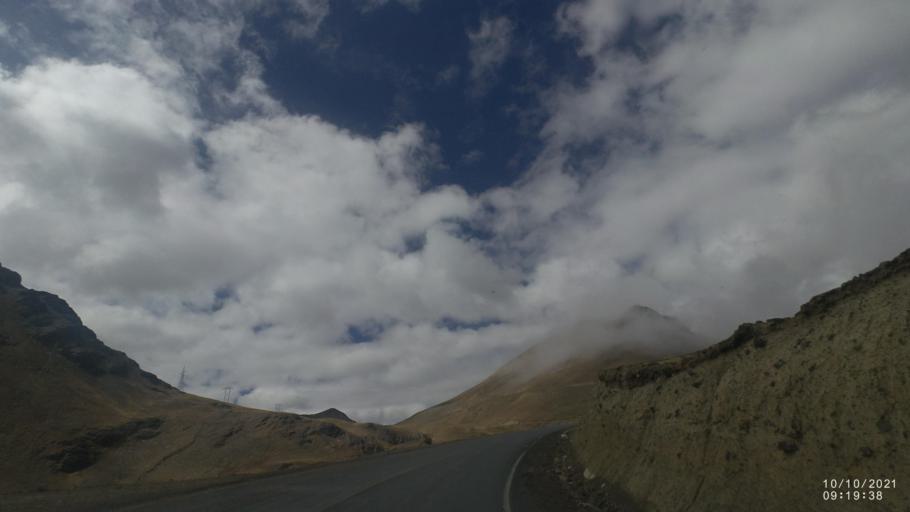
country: BO
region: La Paz
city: Quime
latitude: -17.0553
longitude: -67.2994
